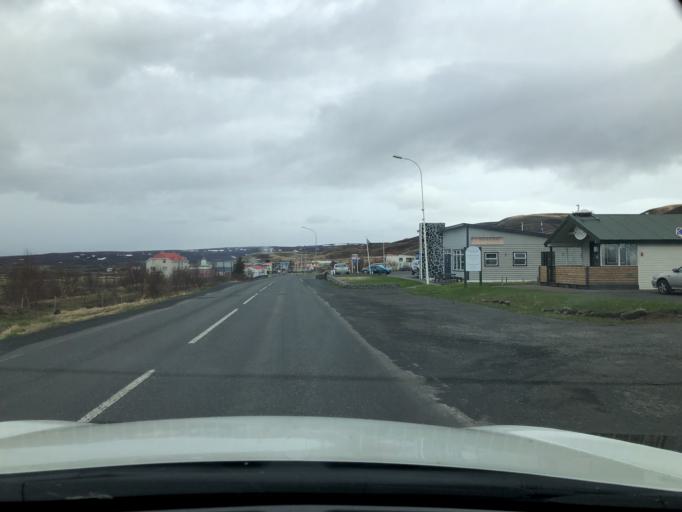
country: IS
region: Northeast
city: Laugar
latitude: 65.6406
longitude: -16.9113
